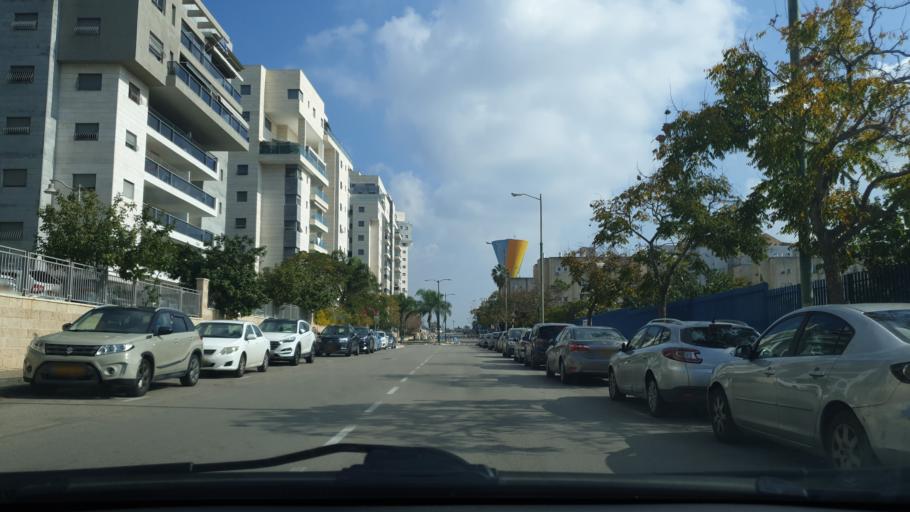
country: IL
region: Central District
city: Bet Dagan
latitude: 31.9683
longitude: 34.8219
